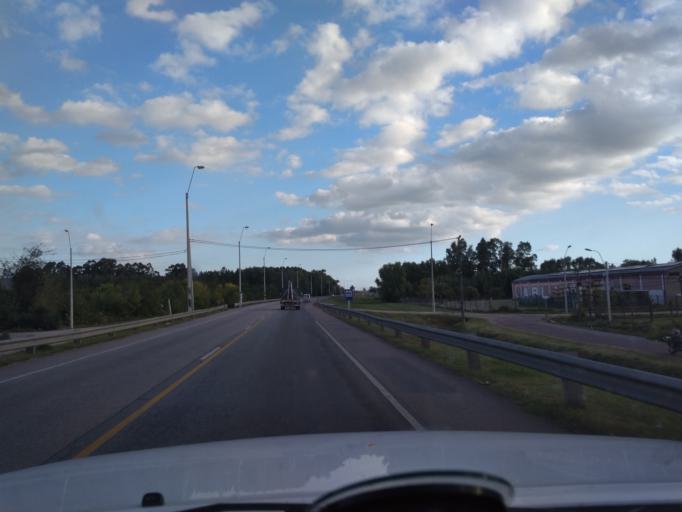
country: UY
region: Canelones
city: Canelones
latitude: -34.5293
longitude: -56.2713
